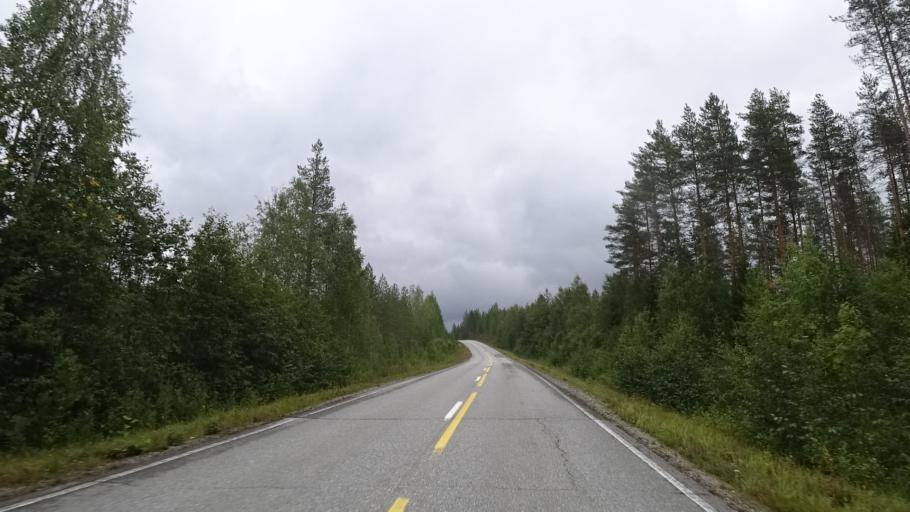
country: FI
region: North Karelia
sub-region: Joensuu
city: Ilomantsi
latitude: 63.2510
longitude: 30.7249
